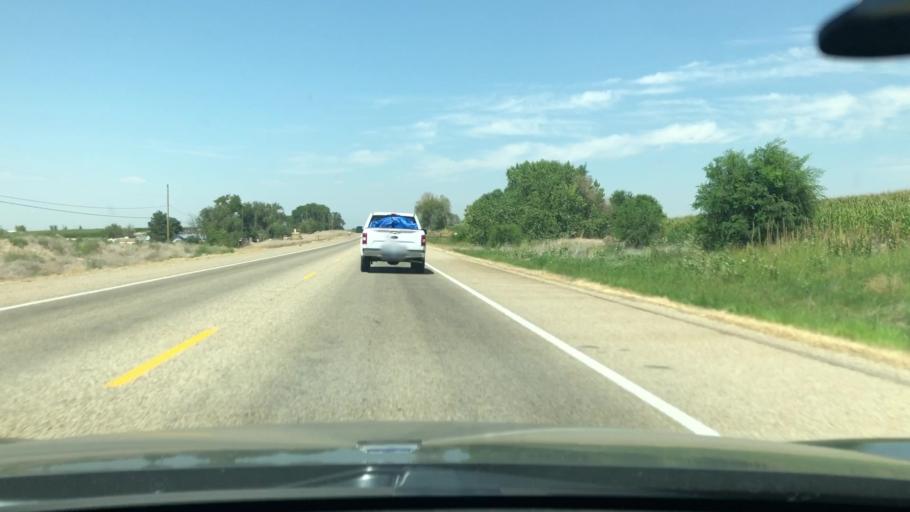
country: US
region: Idaho
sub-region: Canyon County
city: Parma
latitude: 43.8316
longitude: -116.9544
